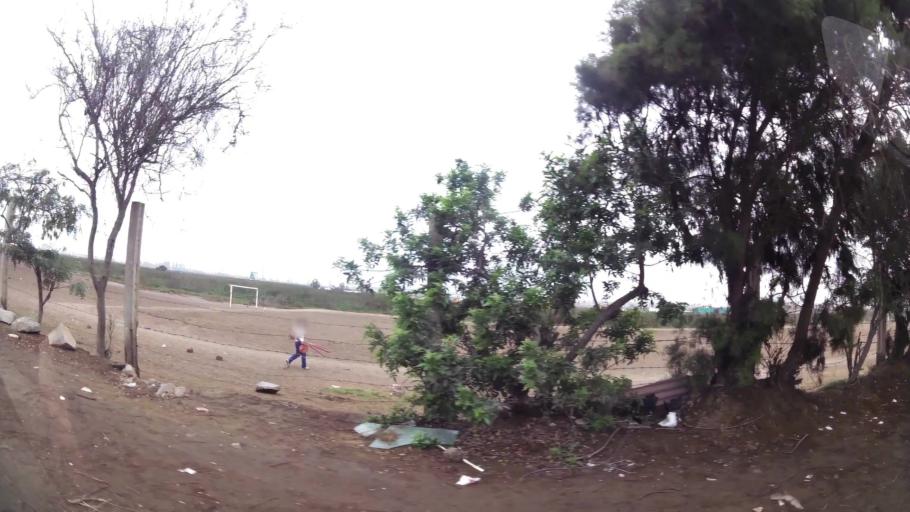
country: PE
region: Lima
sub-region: Lima
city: Surco
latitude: -12.2008
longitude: -76.9927
